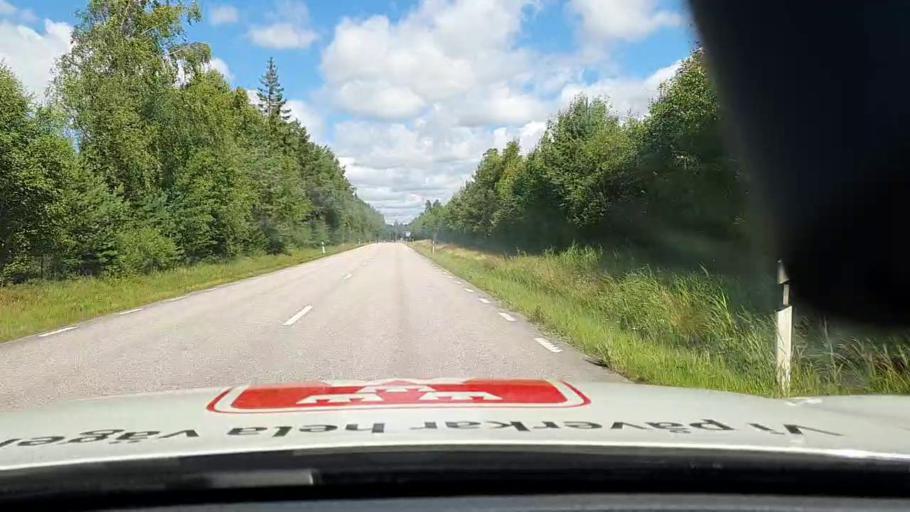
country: SE
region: Vaestra Goetaland
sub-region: Skovde Kommun
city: Stopen
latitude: 58.4477
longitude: 13.9440
